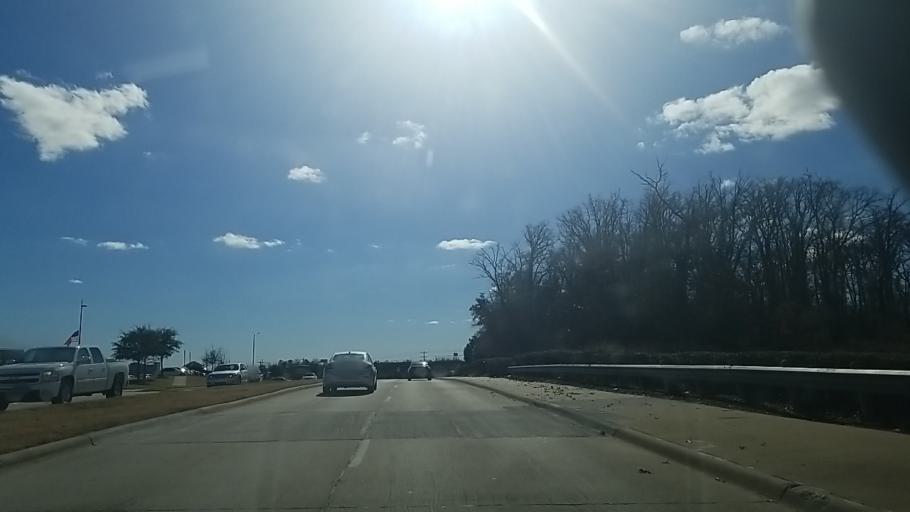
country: US
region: Texas
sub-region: Denton County
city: Corinth
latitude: 33.1878
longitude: -97.0959
